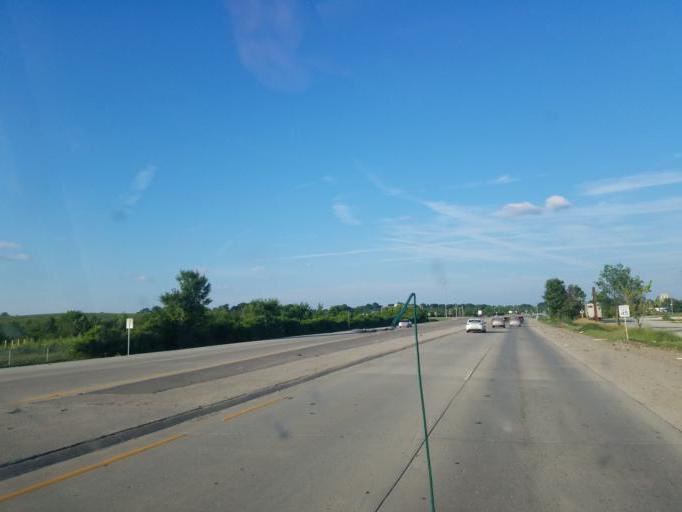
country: US
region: Kentucky
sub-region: Jefferson County
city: Heritage Creek
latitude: 38.1355
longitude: -85.7168
